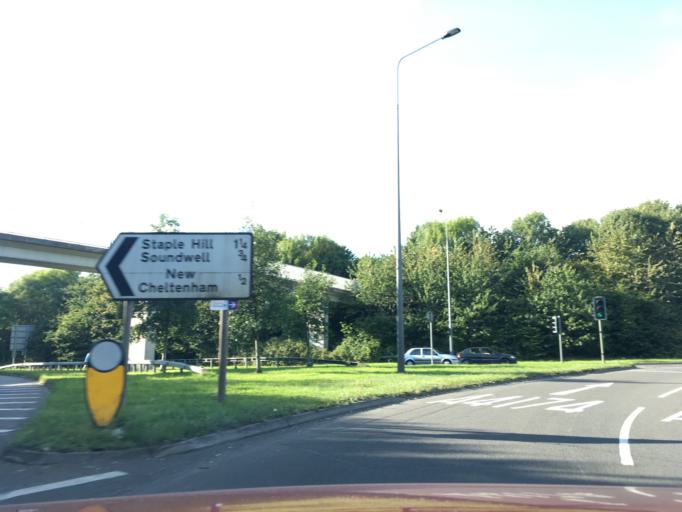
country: GB
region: England
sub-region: South Gloucestershire
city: Mangotsfield
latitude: 51.4705
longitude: -2.4832
